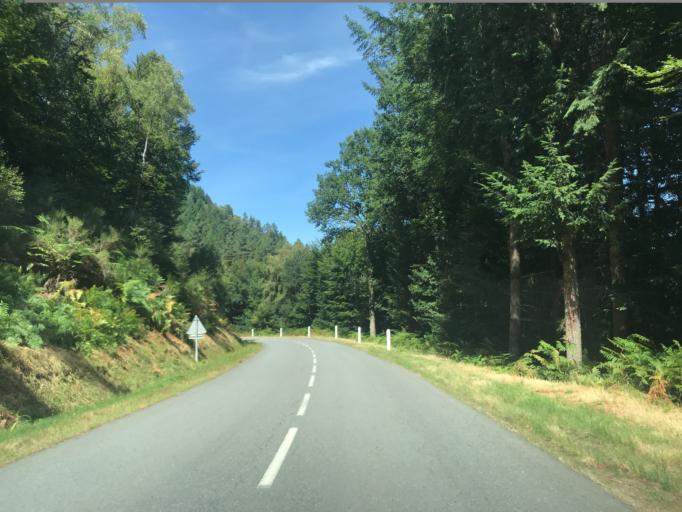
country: FR
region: Limousin
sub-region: Departement de la Creuse
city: Felletin
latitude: 45.7895
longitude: 2.1484
